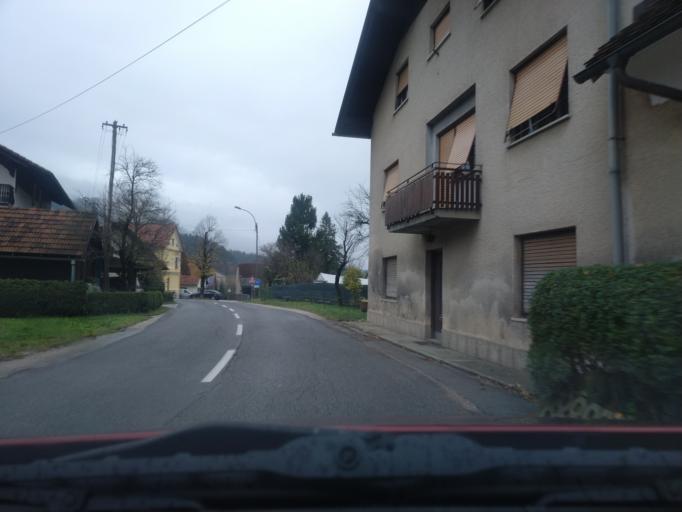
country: SI
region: Gornji Grad
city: Gornji Grad
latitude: 46.2949
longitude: 14.8072
